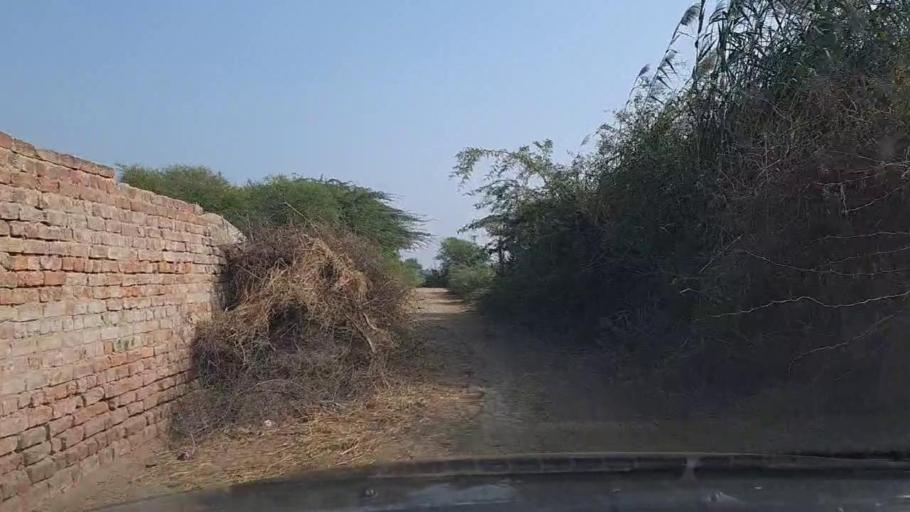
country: PK
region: Sindh
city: Mirpur Batoro
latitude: 24.6964
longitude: 68.2481
